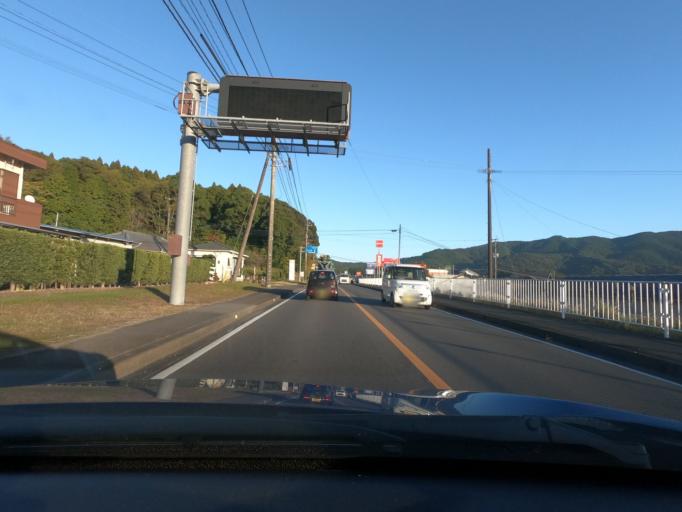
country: JP
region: Kagoshima
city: Satsumasendai
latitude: 31.8072
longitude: 130.3418
